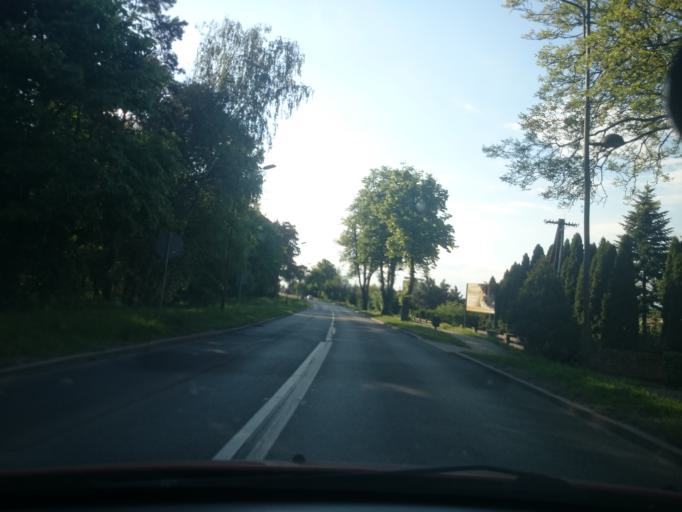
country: PL
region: Opole Voivodeship
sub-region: Powiat strzelecki
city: Strzelce Opolskie
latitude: 50.5189
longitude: 18.2857
